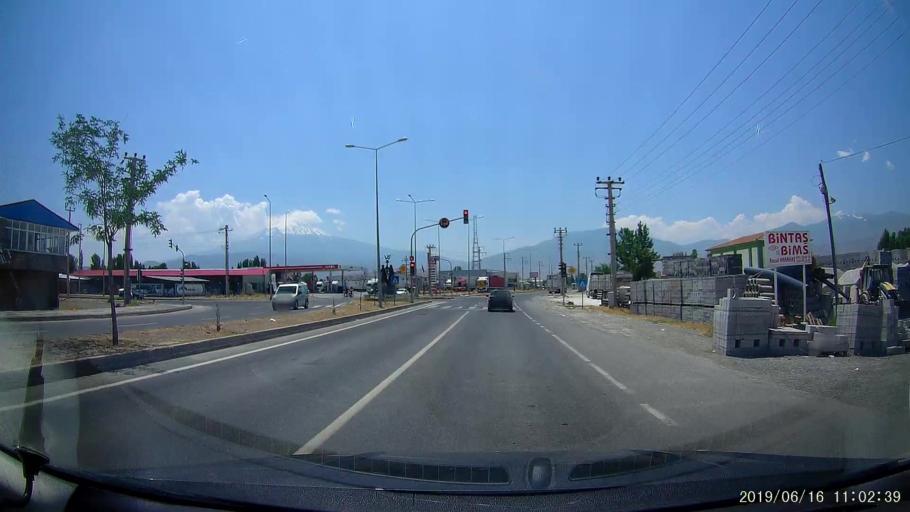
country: TR
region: Igdir
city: Igdir
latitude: 39.9097
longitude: 44.0590
